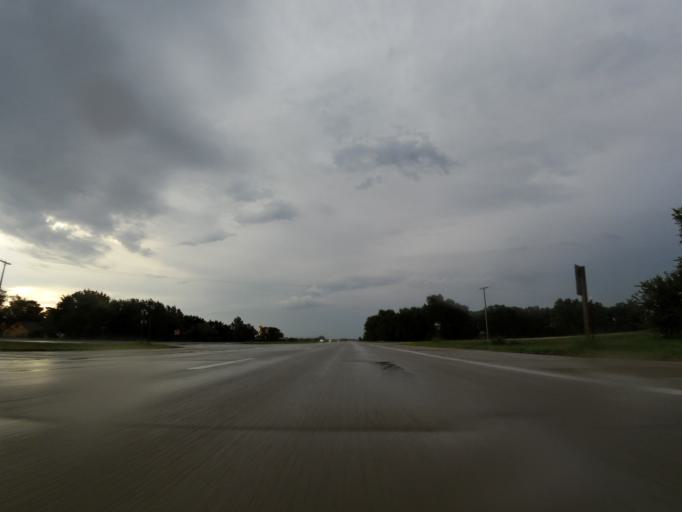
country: US
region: Kansas
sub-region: Reno County
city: Haven
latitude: 37.8819
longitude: -97.7205
